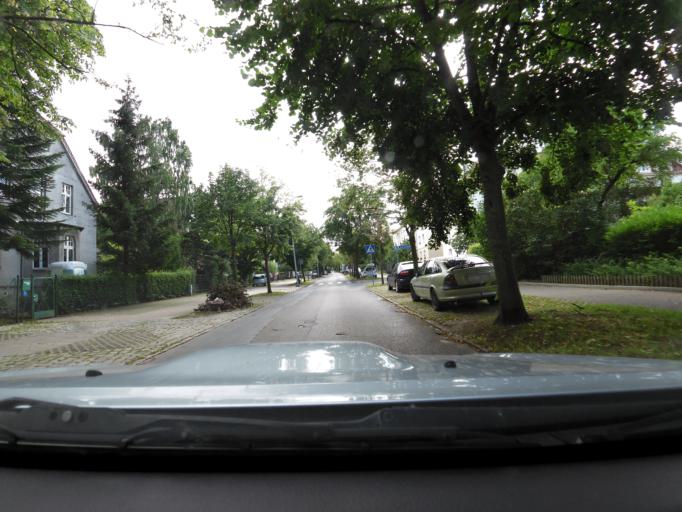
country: PL
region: Pomeranian Voivodeship
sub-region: Sopot
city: Sopot
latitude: 54.4338
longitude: 18.5689
